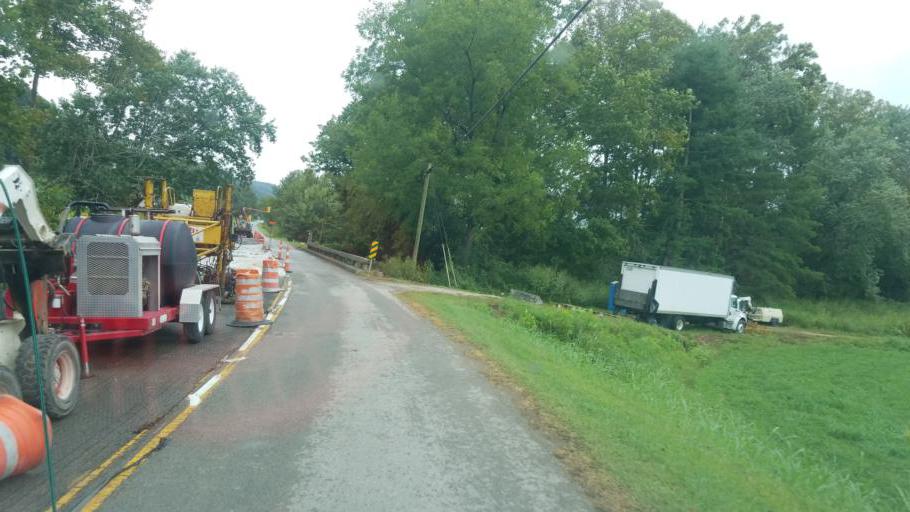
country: US
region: Kentucky
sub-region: Rowan County
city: Morehead
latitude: 38.3453
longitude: -83.5333
